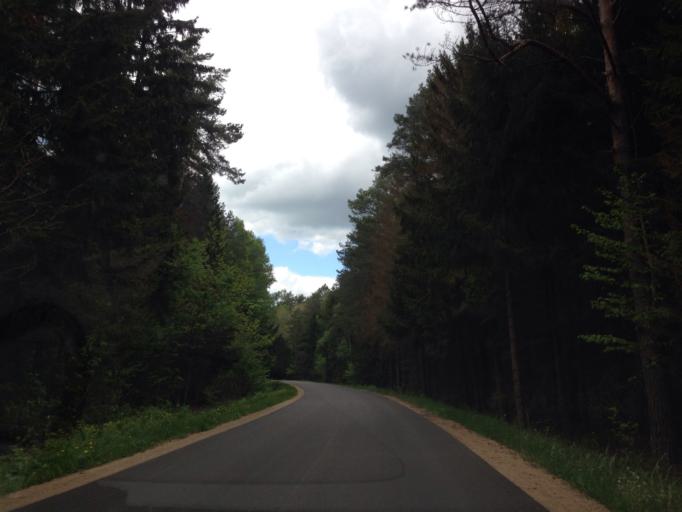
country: PL
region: Podlasie
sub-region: Powiat moniecki
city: Goniadz
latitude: 53.3612
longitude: 22.5996
